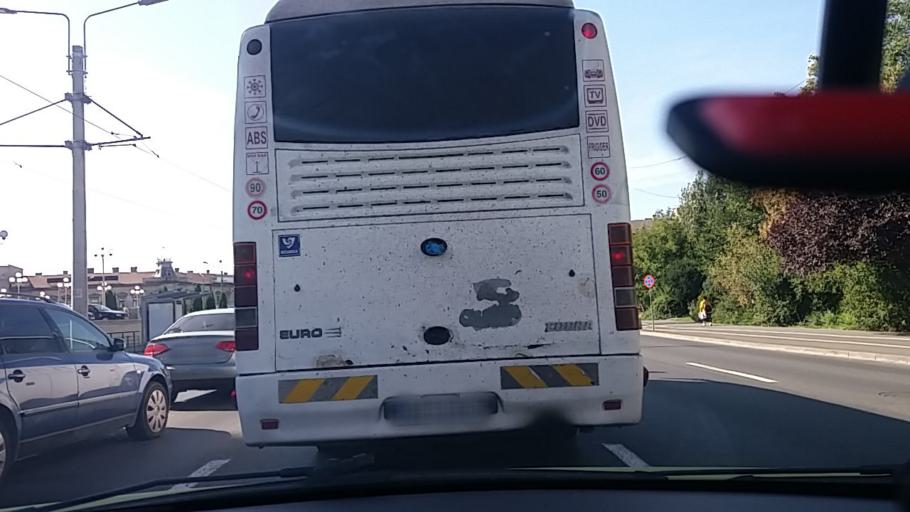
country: RO
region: Arad
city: Arad
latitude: 46.1840
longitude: 21.3243
